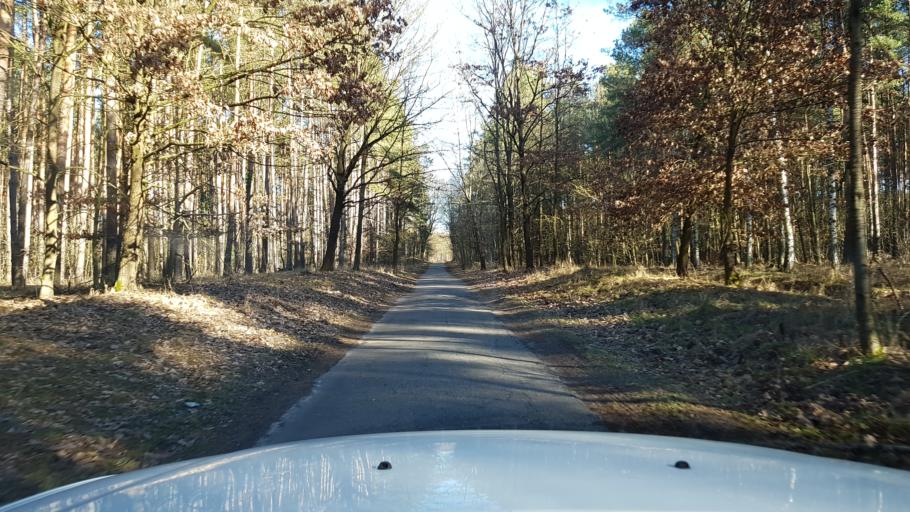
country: PL
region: West Pomeranian Voivodeship
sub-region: Powiat pyrzycki
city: Lipiany
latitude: 53.0183
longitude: 15.0032
